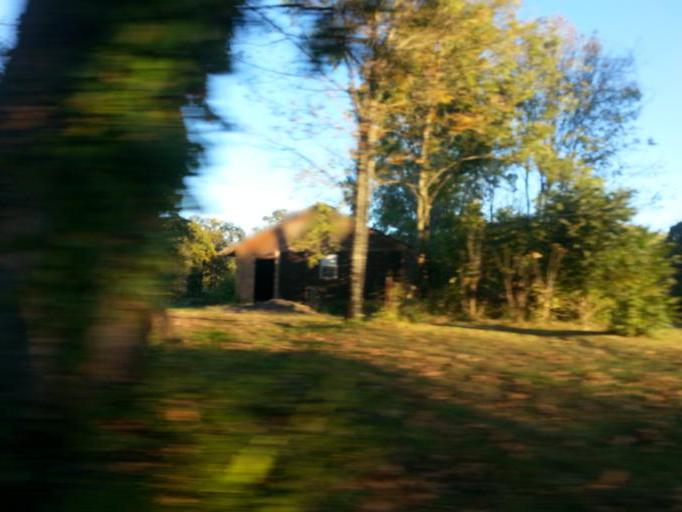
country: US
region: Tennessee
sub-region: Blount County
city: Wildwood
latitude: 35.7987
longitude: -83.8121
